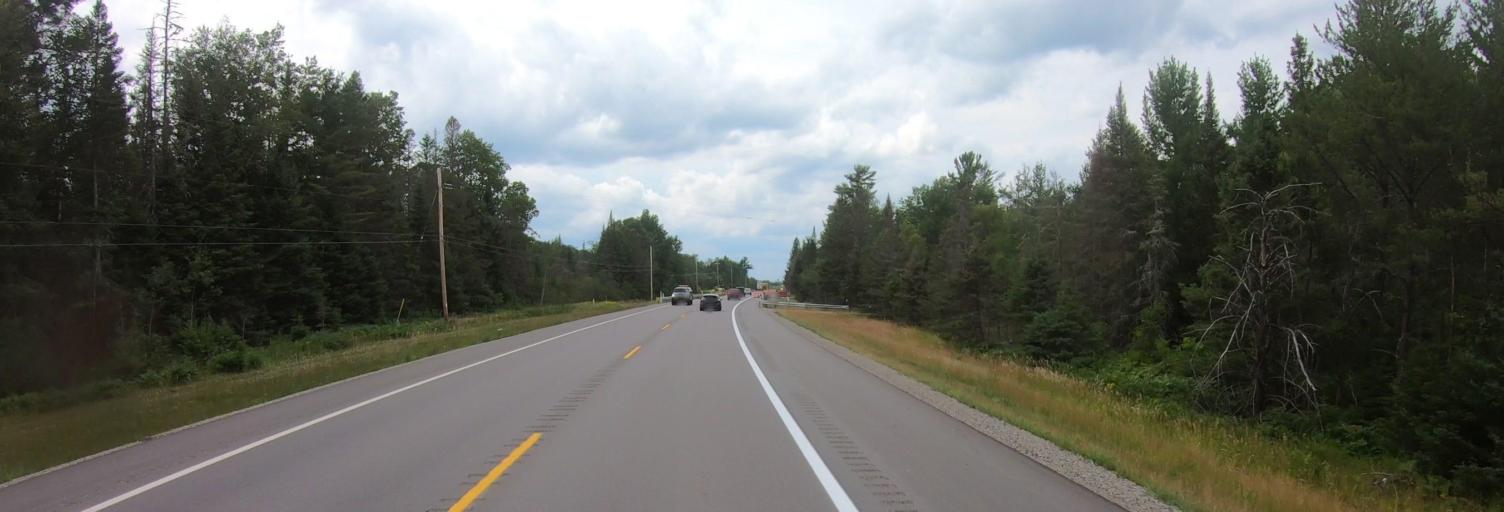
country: US
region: Michigan
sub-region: Baraga County
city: L'Anse
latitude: 46.5543
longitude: -88.2176
